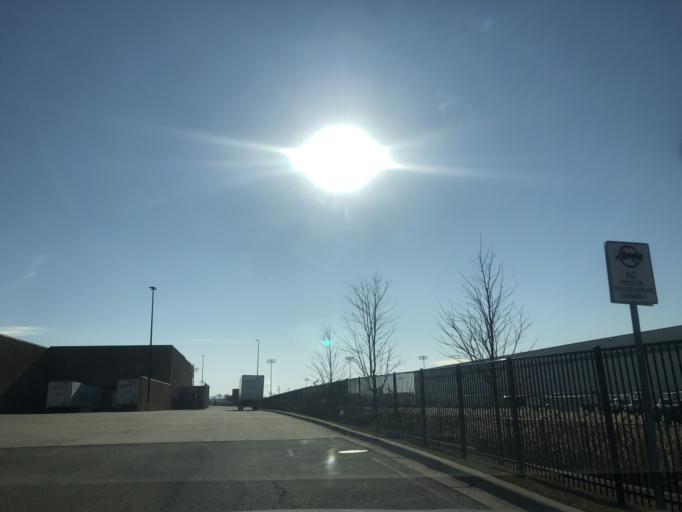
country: US
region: Illinois
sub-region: Cook County
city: Cicero
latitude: 41.8319
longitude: -87.7482
